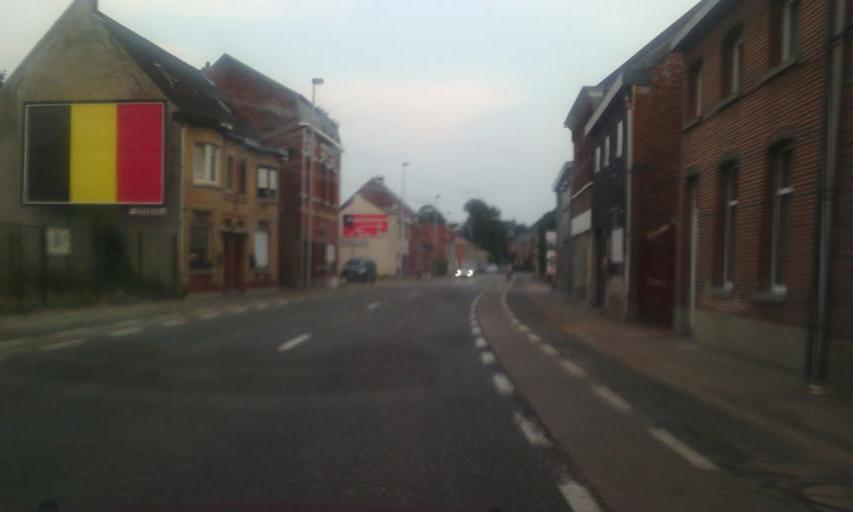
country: BE
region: Flanders
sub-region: Provincie Oost-Vlaanderen
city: Dendermonde
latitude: 51.0487
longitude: 4.1077
